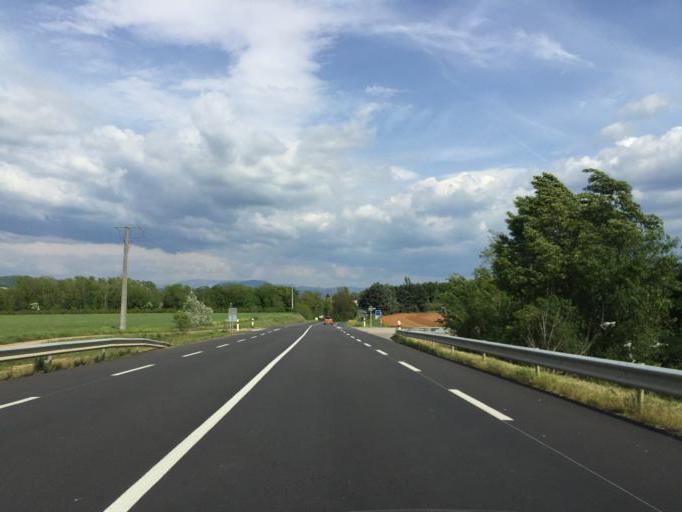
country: FR
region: Rhone-Alpes
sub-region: Departement de la Drome
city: Eurre
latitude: 44.7231
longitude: 4.9770
